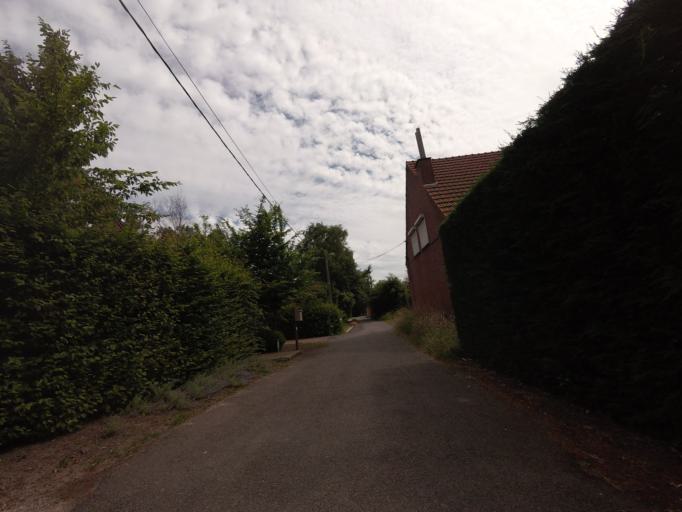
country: BE
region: Flanders
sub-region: Provincie Antwerpen
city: Rumst
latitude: 51.0828
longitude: 4.4620
